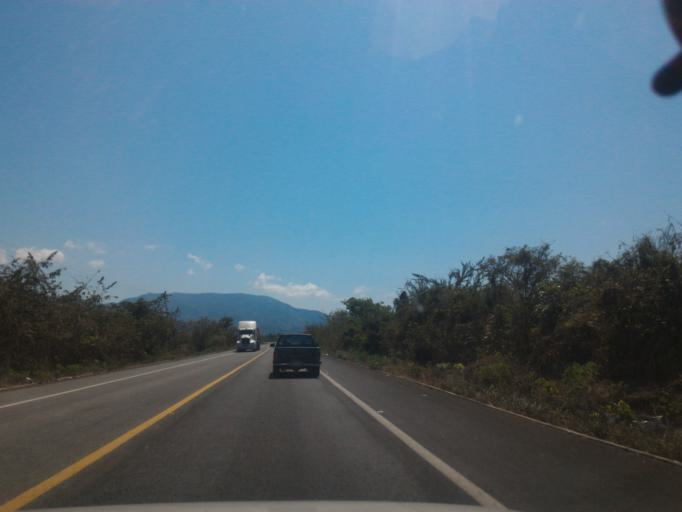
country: MX
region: Michoacan
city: Coahuayana Viejo
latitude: 18.6864
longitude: -103.6965
